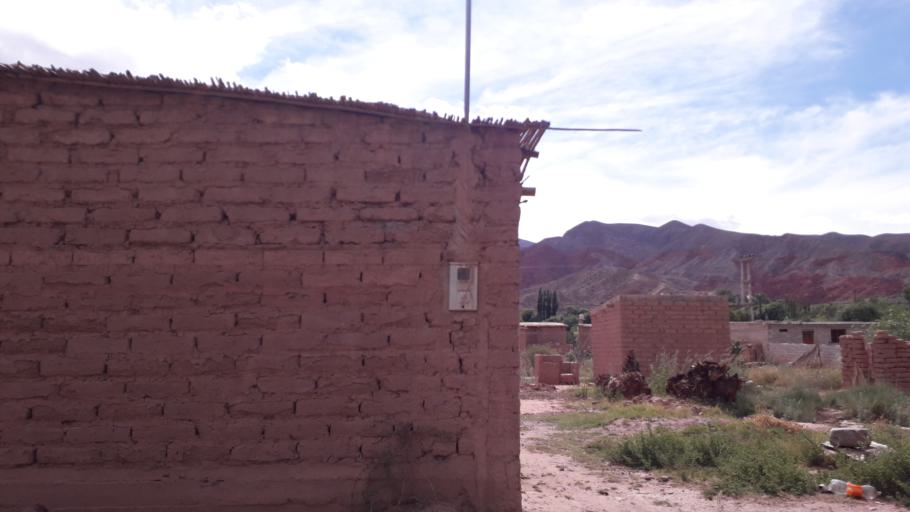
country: AR
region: Jujuy
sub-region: Departamento de Humahuaca
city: Humahuaca
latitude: -23.3070
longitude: -65.3531
